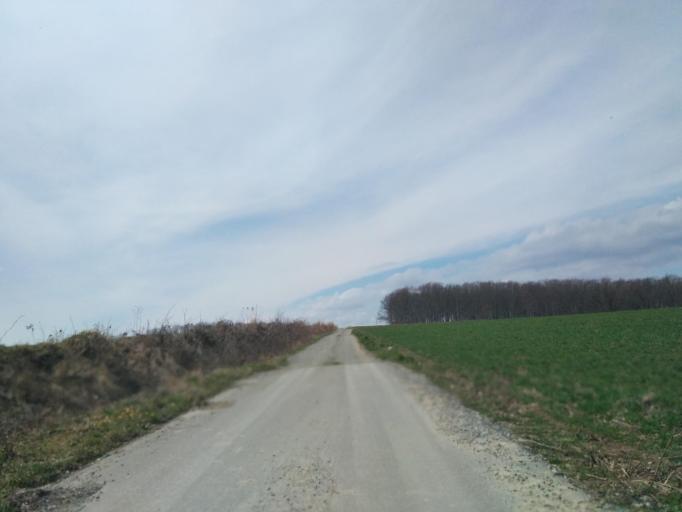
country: PL
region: Subcarpathian Voivodeship
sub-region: Powiat ropczycko-sedziszowski
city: Iwierzyce
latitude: 50.0396
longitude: 21.7323
